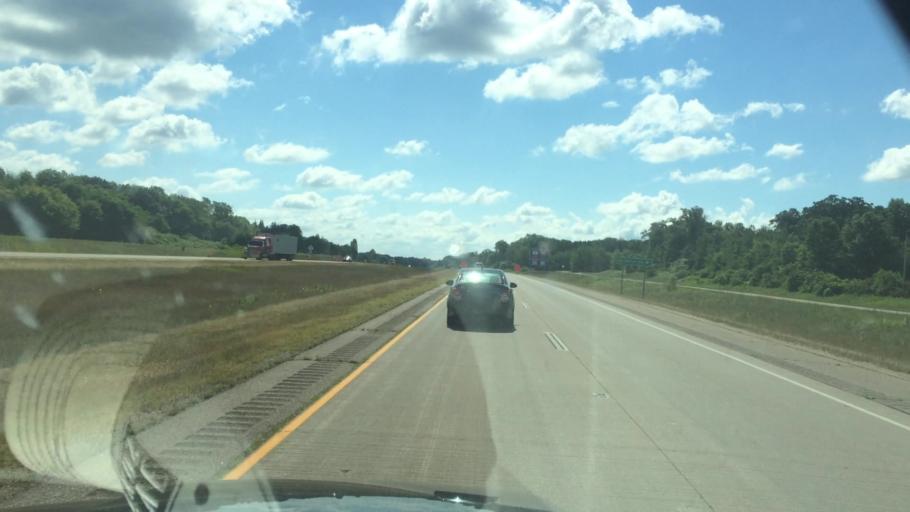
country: US
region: Wisconsin
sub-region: Waupaca County
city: King
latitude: 44.3674
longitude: -89.1423
